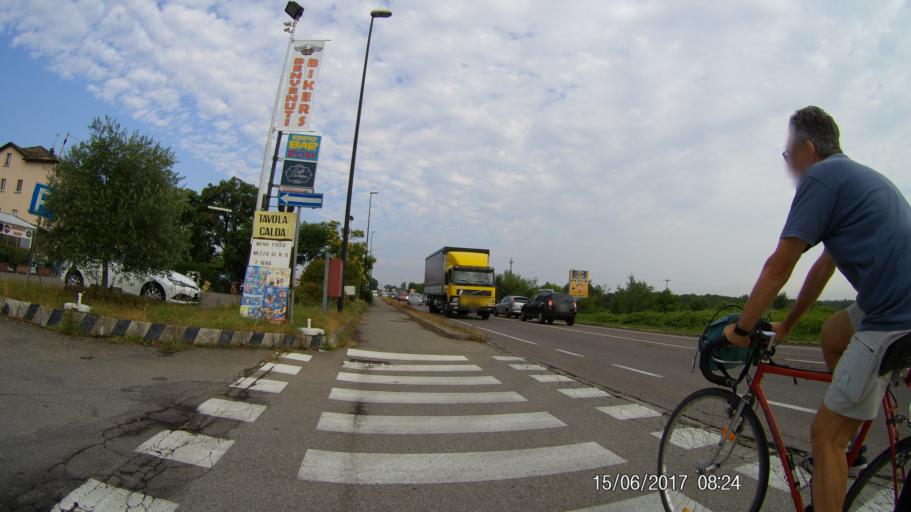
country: IT
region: Emilia-Romagna
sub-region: Provincia di Reggio Emilia
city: Roncocesi
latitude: 44.7219
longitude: 10.5639
